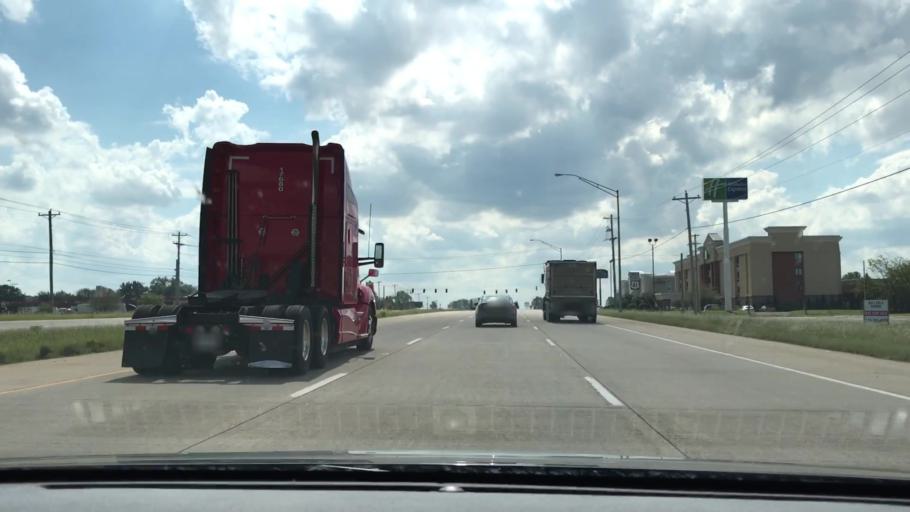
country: US
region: Kentucky
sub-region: Christian County
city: Oak Grove
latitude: 36.6956
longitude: -87.4533
